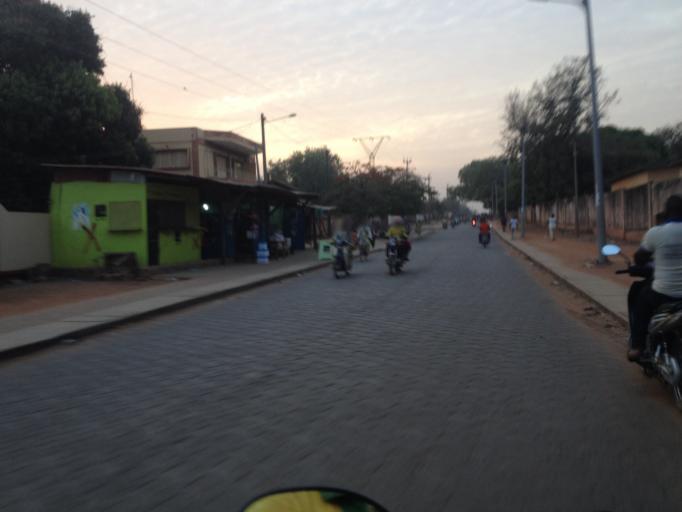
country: BJ
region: Borgou
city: Parakou
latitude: 9.3366
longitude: 2.6388
